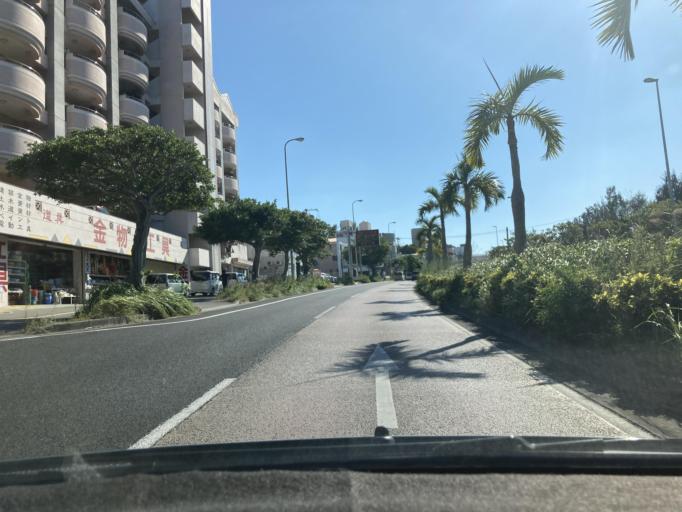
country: JP
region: Okinawa
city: Naha-shi
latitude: 26.1996
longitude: 127.6618
